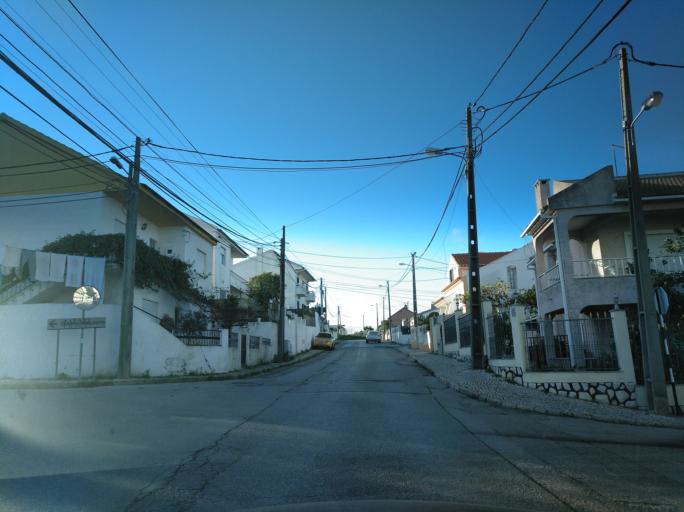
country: PT
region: Setubal
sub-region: Almada
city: Sobreda
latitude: 38.6450
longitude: -9.1872
